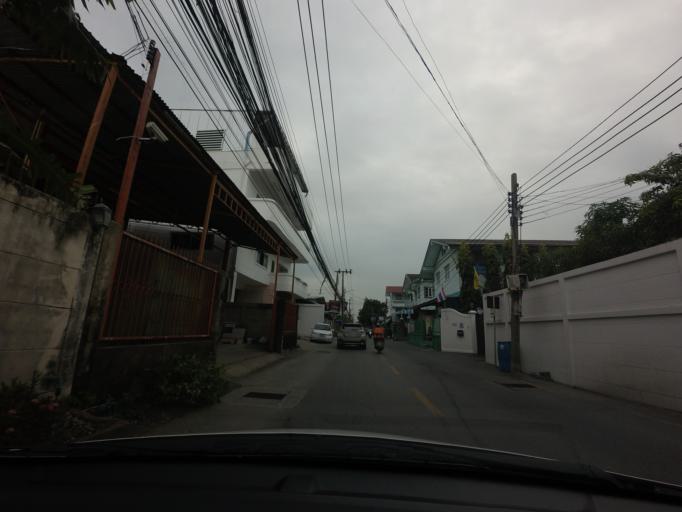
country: TH
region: Bangkok
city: Suan Luang
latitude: 13.7184
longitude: 100.6377
